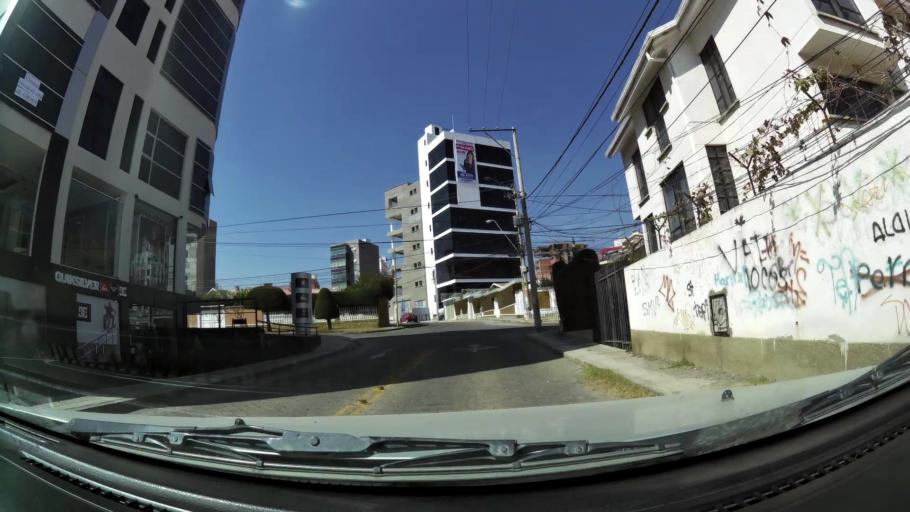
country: BO
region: La Paz
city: La Paz
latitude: -16.5445
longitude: -68.0798
